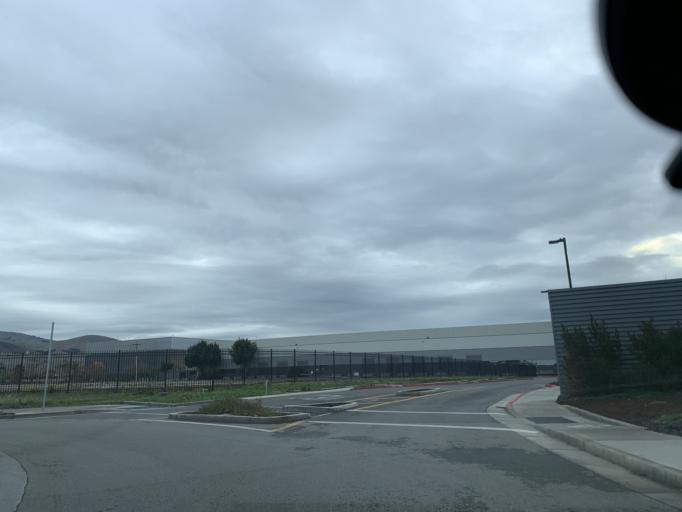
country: US
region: California
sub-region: Santa Clara County
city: Seven Trees
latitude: 37.2421
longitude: -121.7852
